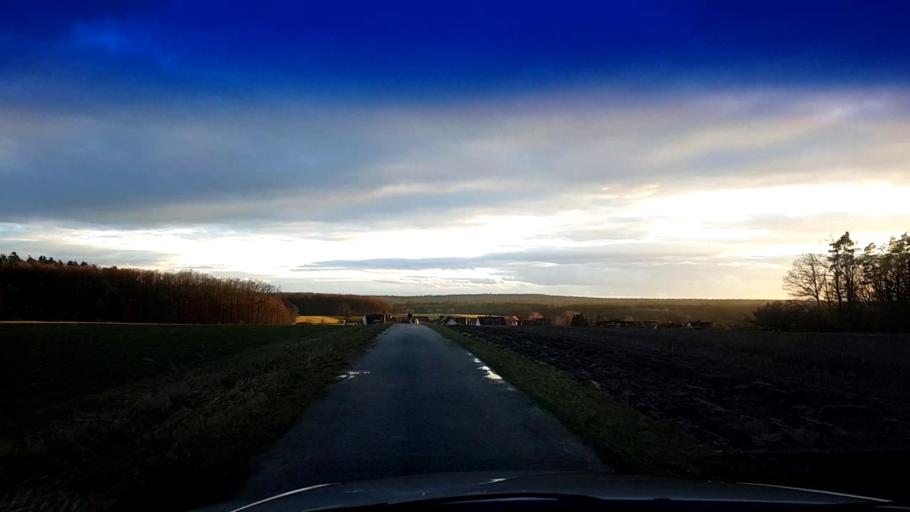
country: DE
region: Bavaria
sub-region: Upper Franconia
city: Memmelsdorf
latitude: 49.9363
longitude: 10.9836
